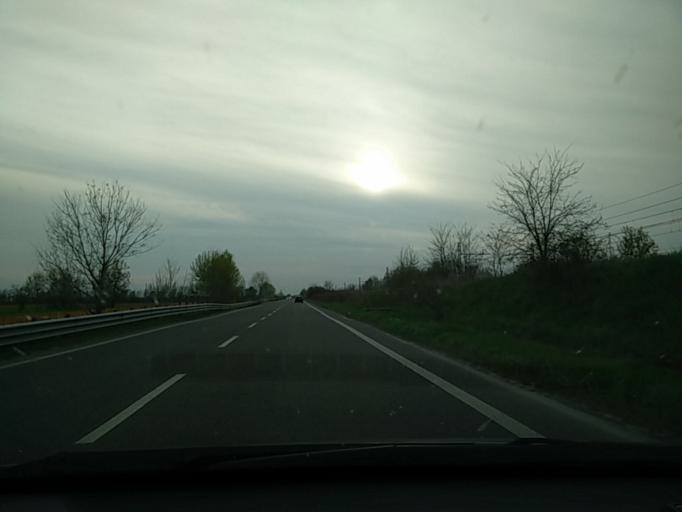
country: IT
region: Lombardy
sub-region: Provincia di Pavia
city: Montebello
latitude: 45.0082
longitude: 9.0907
